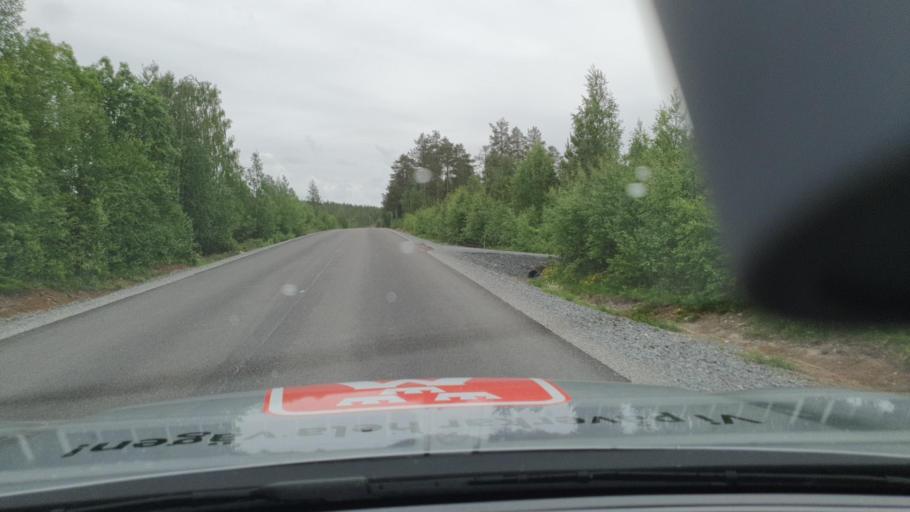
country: SE
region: Norrbotten
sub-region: Overtornea Kommun
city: OEvertornea
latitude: 66.6055
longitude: 23.2987
